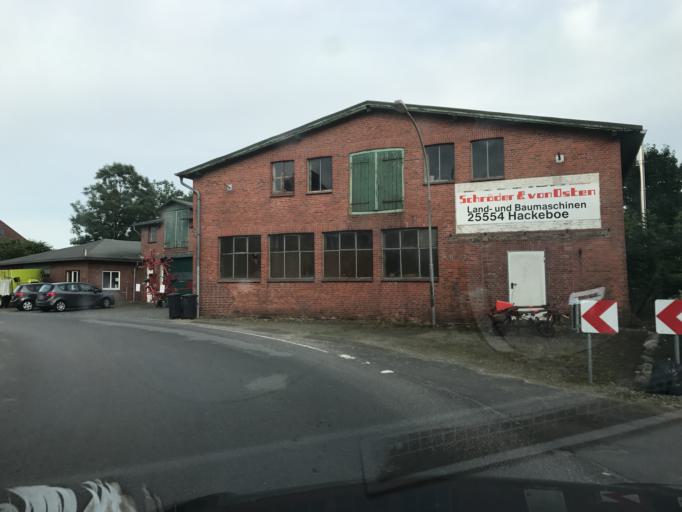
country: DE
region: Schleswig-Holstein
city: Landrecht
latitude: 53.9473
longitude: 9.3491
